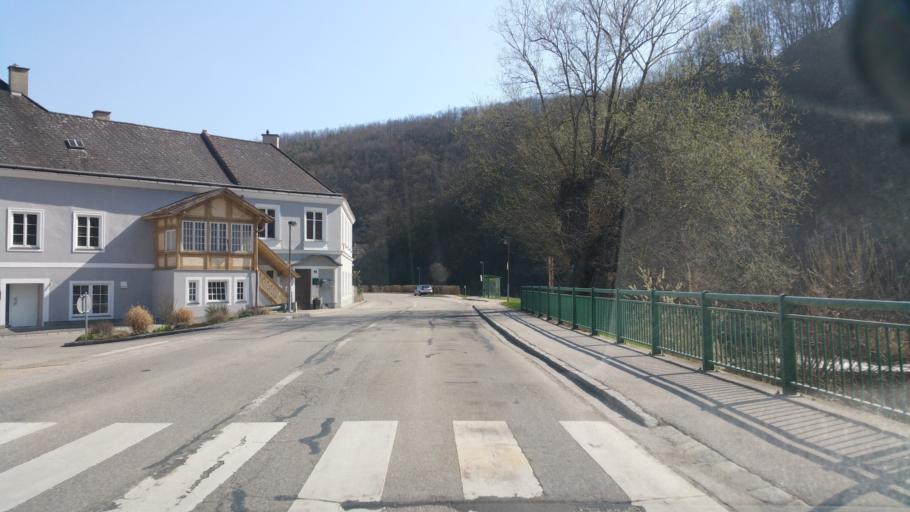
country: AT
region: Lower Austria
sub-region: Politischer Bezirk Krems
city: Senftenberg
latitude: 48.4395
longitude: 15.5753
